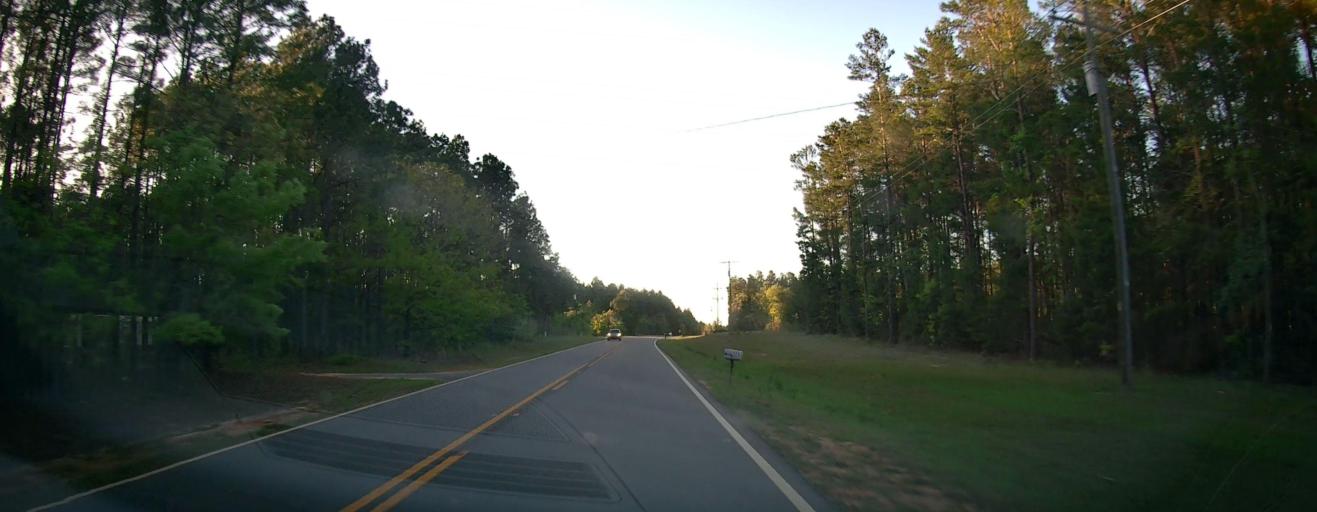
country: US
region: Georgia
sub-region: Talbot County
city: Talbotton
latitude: 32.5030
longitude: -84.4655
